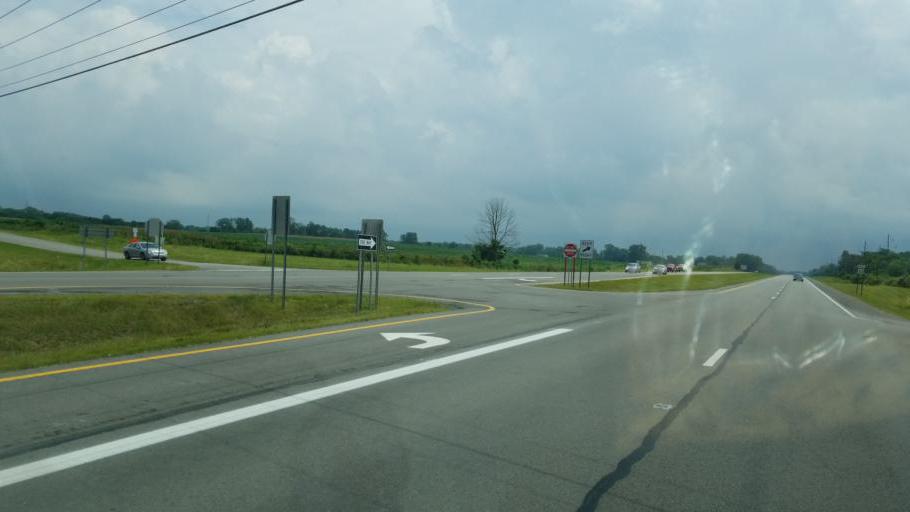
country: US
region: Ohio
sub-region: Logan County
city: Bellefontaine
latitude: 40.4295
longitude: -83.8014
